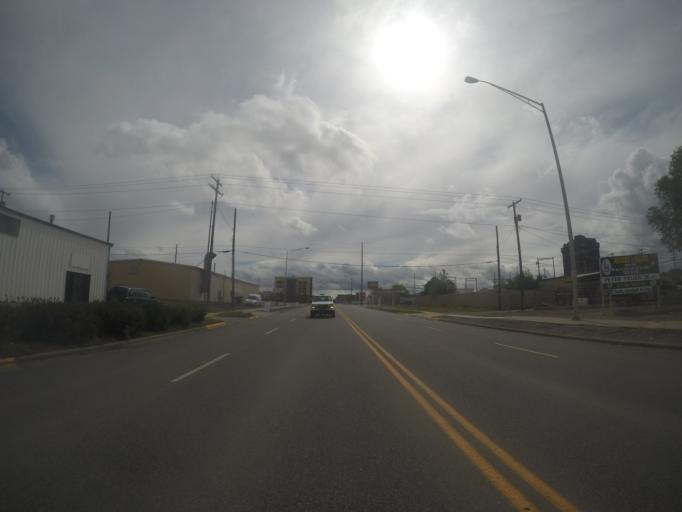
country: US
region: Montana
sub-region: Yellowstone County
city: Billings
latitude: 45.7818
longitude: -108.4986
